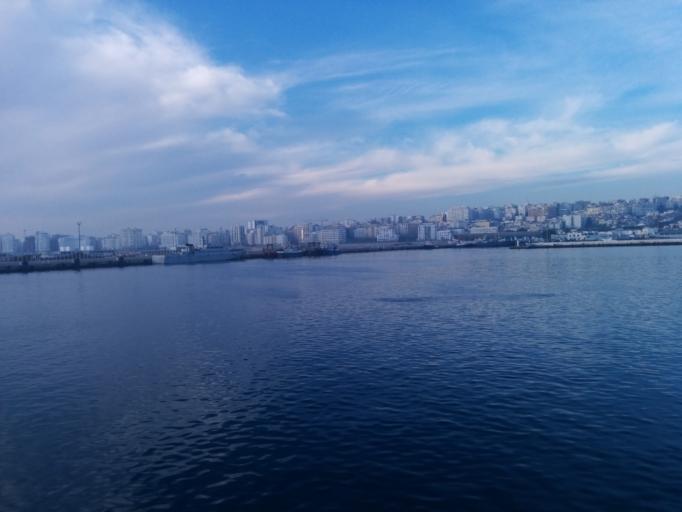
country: MA
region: Tanger-Tetouan
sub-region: Tanger-Assilah
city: Tangier
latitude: 35.7904
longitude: -5.7998
